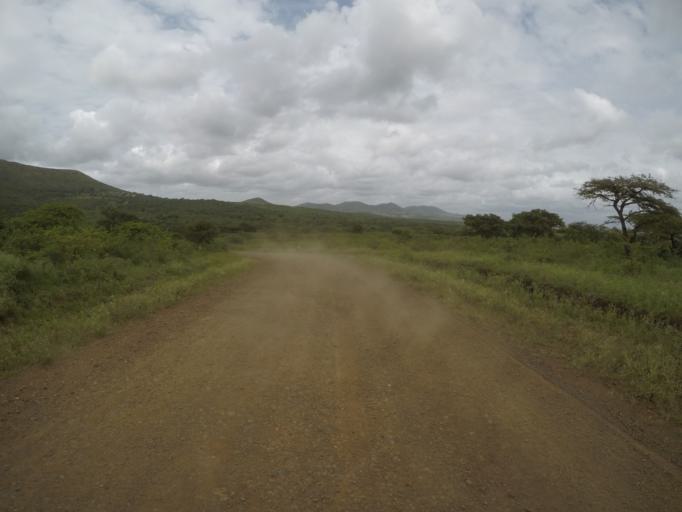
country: ZA
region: KwaZulu-Natal
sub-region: uThungulu District Municipality
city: Empangeni
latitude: -28.5938
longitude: 31.8906
